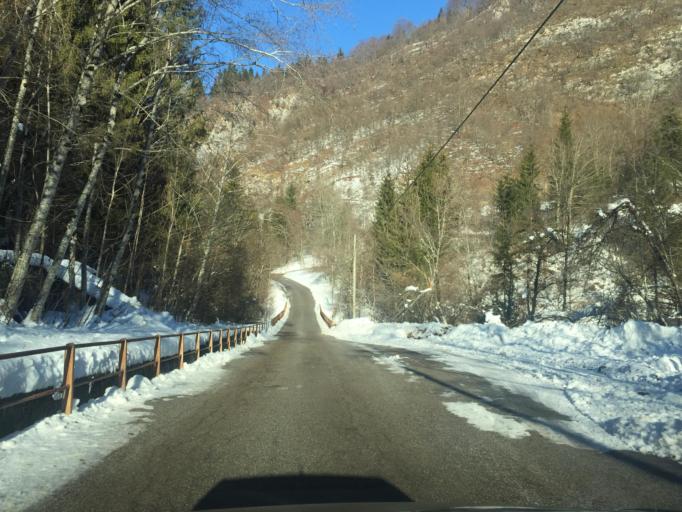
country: IT
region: Friuli Venezia Giulia
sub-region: Provincia di Udine
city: Lauco
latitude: 46.4432
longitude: 12.9499
